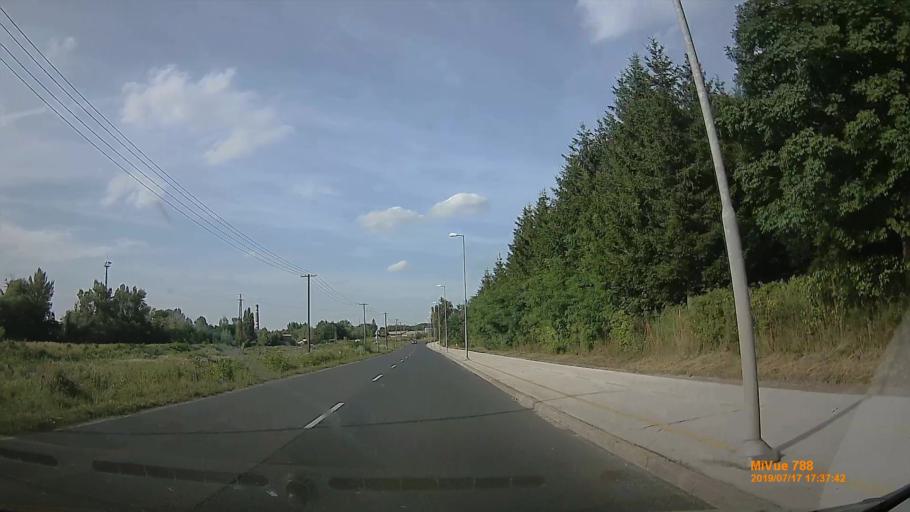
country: HU
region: Veszprem
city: Ajka
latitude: 47.0830
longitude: 17.5485
